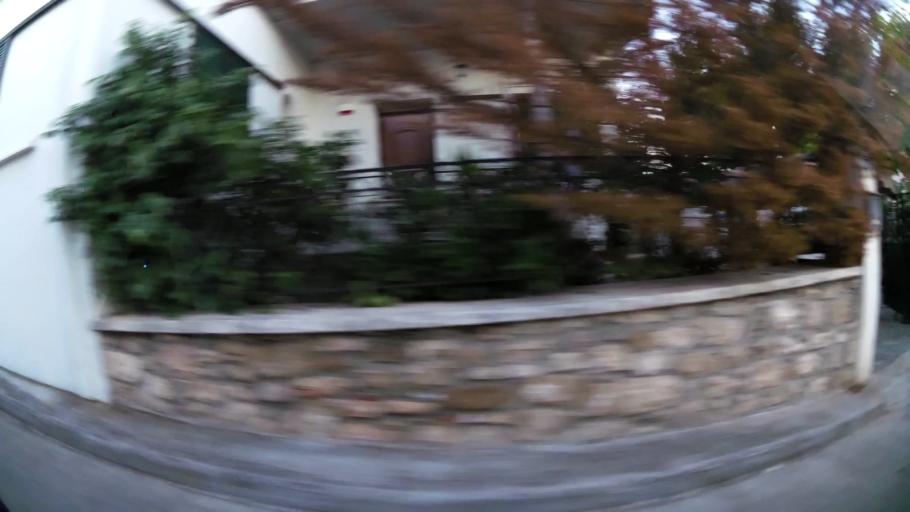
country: GR
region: Attica
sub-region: Nomarchia Anatolikis Attikis
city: Spata
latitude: 37.9637
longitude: 23.9111
